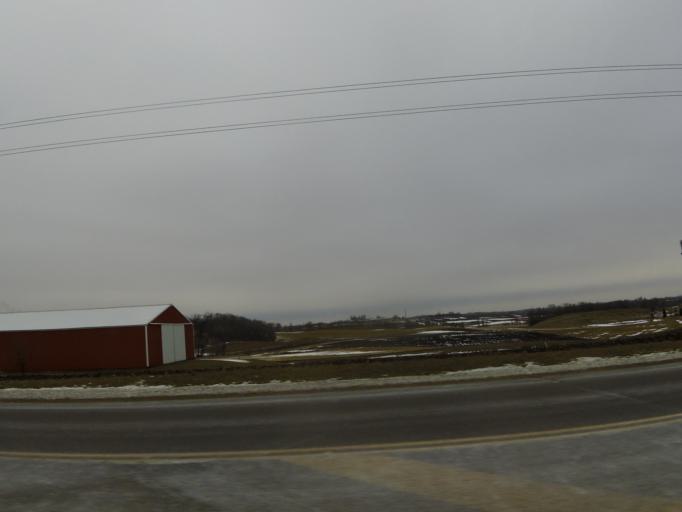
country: US
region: Minnesota
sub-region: Carver County
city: Carver
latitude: 44.7764
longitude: -93.6860
